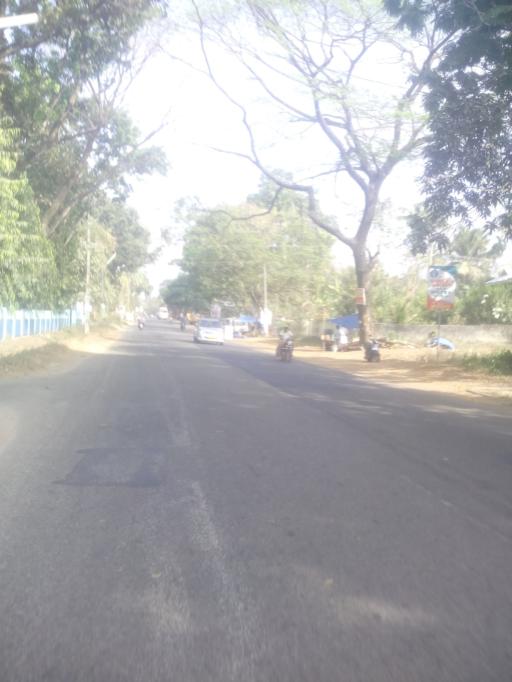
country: IN
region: Kerala
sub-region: Ernakulam
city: Perumpavur
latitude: 10.1133
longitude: 76.5090
